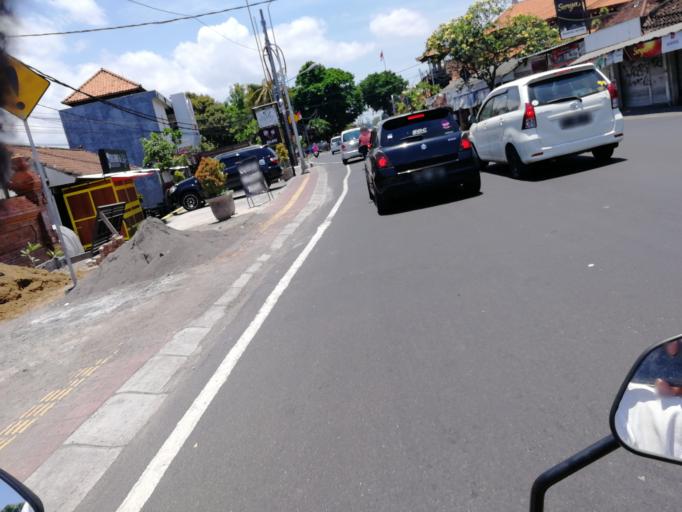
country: ID
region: Bali
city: Karyadharma
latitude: -8.6886
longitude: 115.1920
